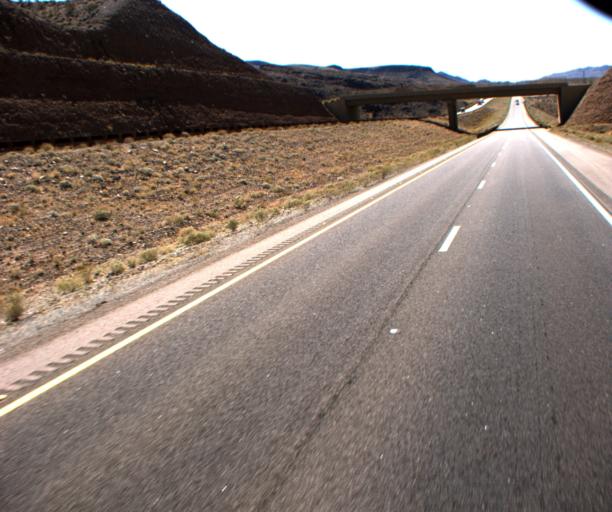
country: US
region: Nevada
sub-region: Clark County
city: Boulder City
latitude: 35.8895
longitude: -114.6222
